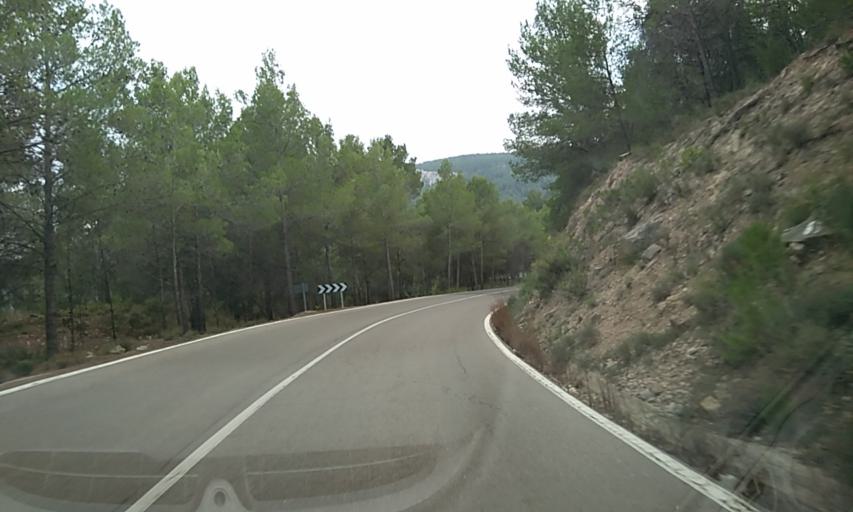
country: ES
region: Valencia
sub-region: Provincia de Castello
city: Puebla de Arenoso
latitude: 40.0936
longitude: -0.5673
